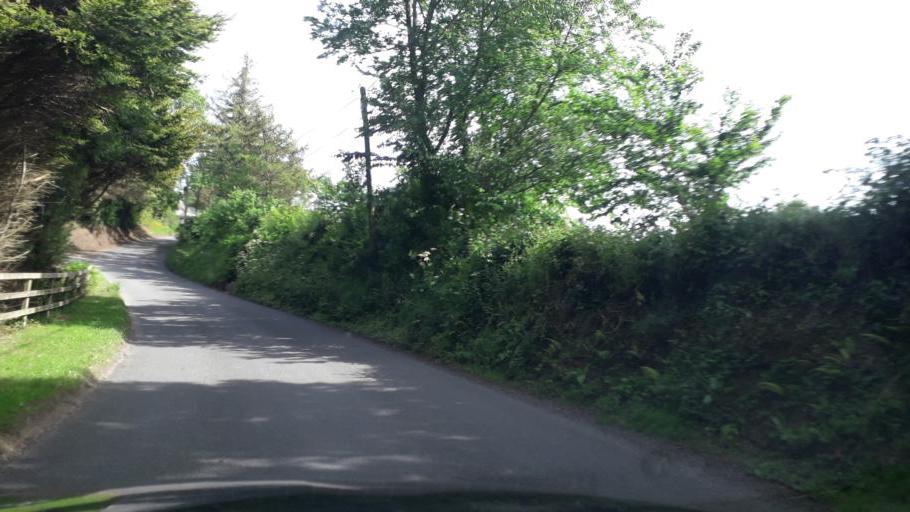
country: IE
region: Leinster
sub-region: Loch Garman
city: Castlebridge
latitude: 52.4053
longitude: -6.4063
